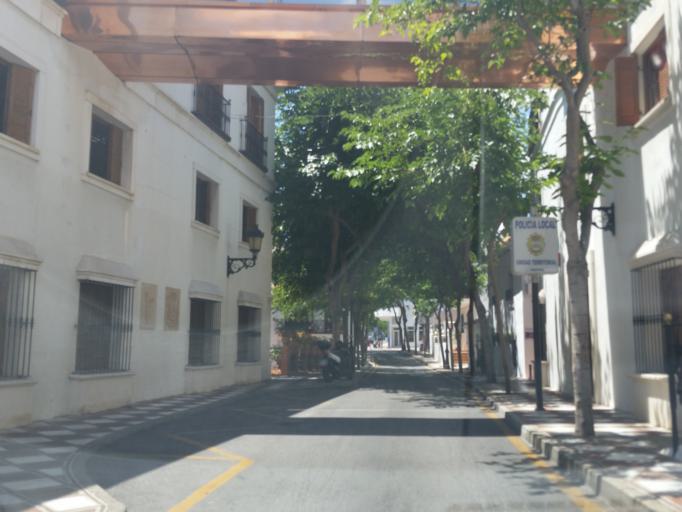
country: ES
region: Andalusia
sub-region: Provincia de Malaga
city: Benalmadena
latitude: 36.5952
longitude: -4.5734
